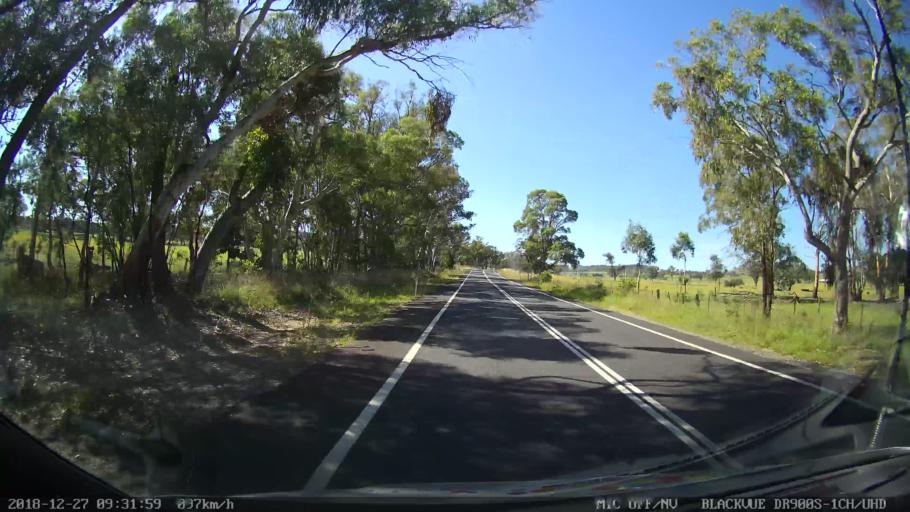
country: AU
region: New South Wales
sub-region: Lithgow
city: Portland
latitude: -33.2008
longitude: 150.0139
